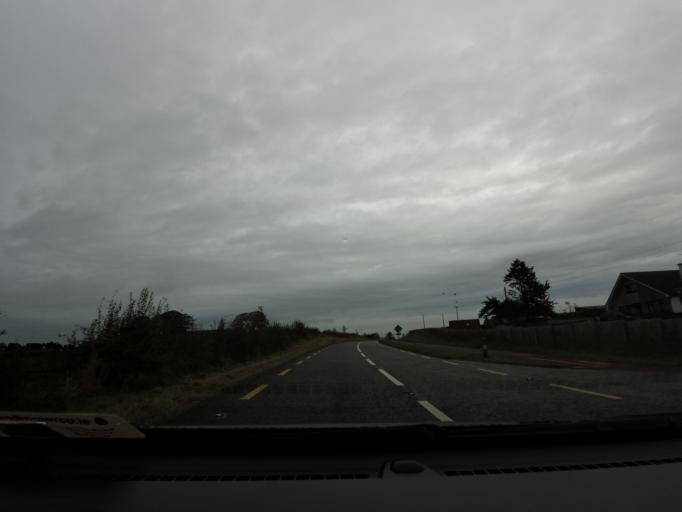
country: IE
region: Connaught
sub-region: County Galway
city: Tuam
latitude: 53.5329
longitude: -8.8297
